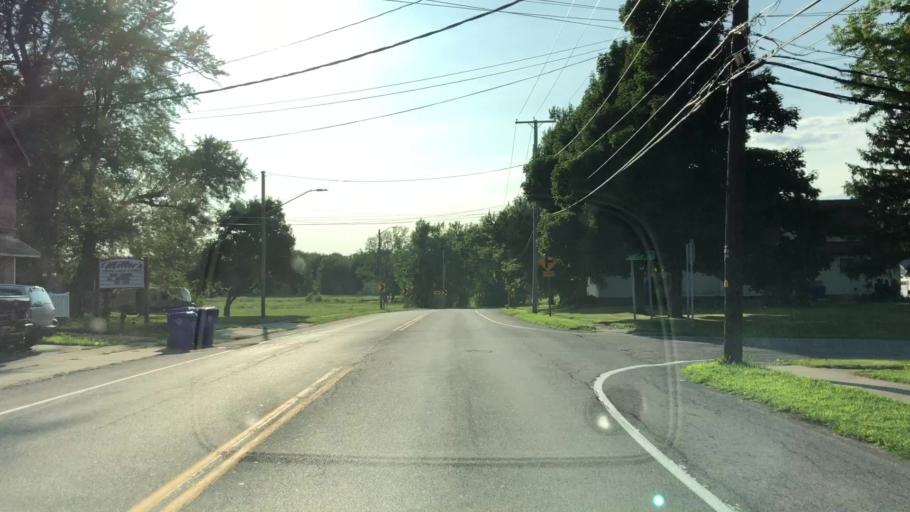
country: US
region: New York
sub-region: Erie County
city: West Seneca
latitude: 42.8563
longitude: -78.7585
